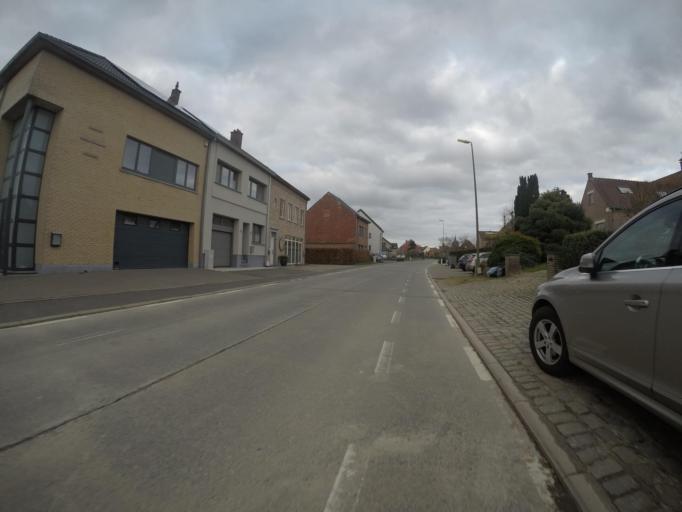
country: BE
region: Flanders
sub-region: Provincie Vlaams-Brabant
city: Pepingen
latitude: 50.7579
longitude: 4.1543
